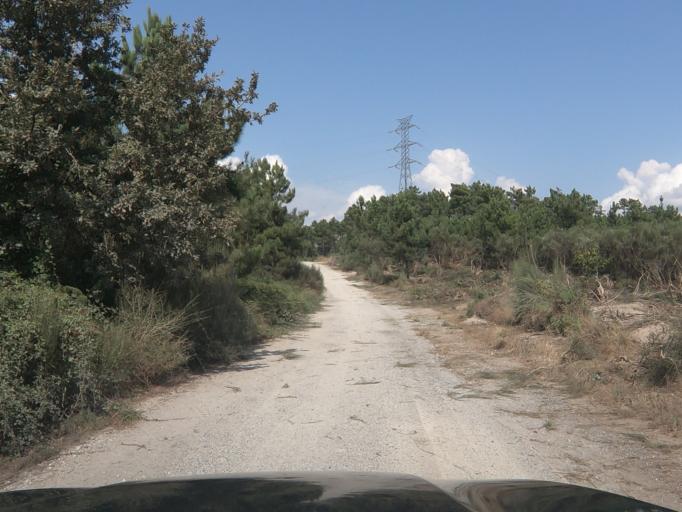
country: PT
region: Vila Real
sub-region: Sabrosa
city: Sabrosa
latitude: 41.3206
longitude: -7.6204
